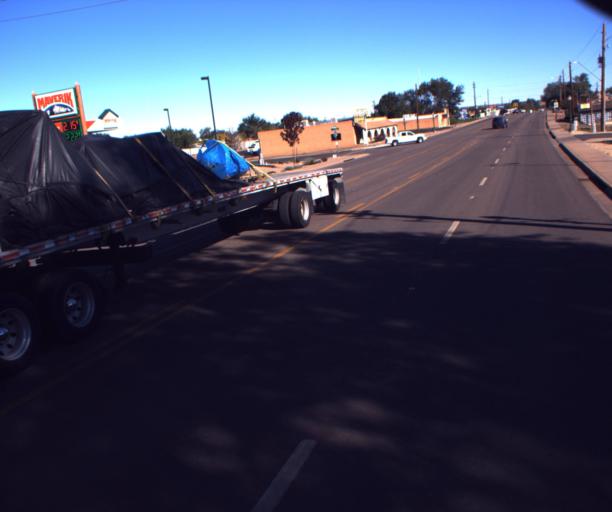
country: US
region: Arizona
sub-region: Navajo County
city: Snowflake
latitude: 34.4990
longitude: -110.0790
